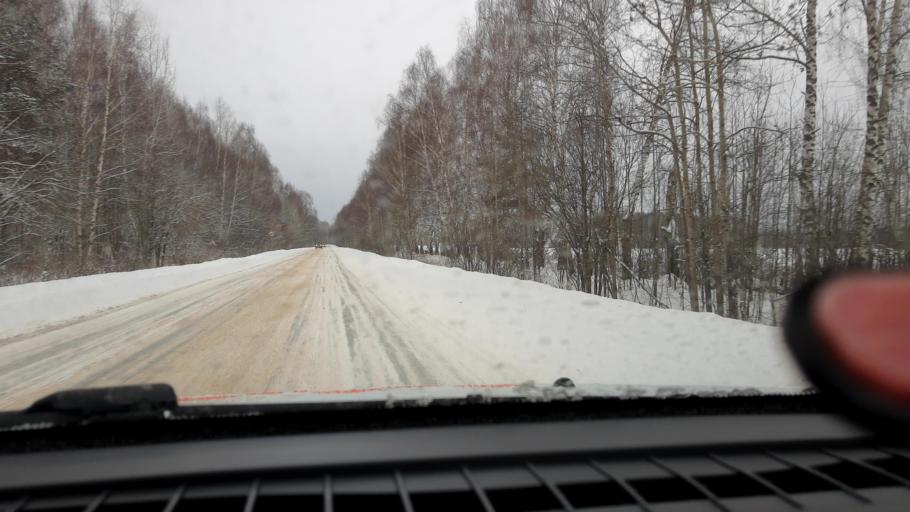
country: RU
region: Nizjnij Novgorod
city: Pamyat' Parizhskoy Kommuny
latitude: 56.2511
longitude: 44.4762
